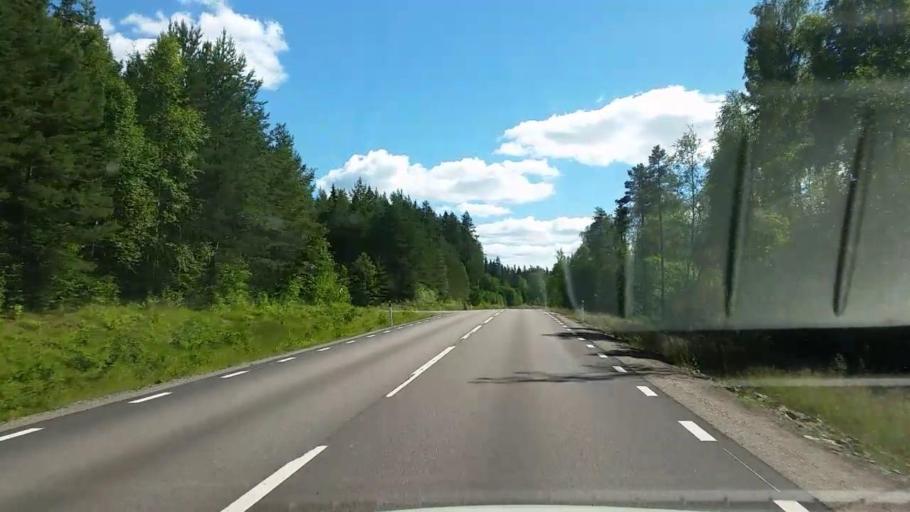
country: SE
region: Dalarna
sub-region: Faluns Kommun
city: Svardsjo
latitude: 60.7698
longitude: 15.7554
